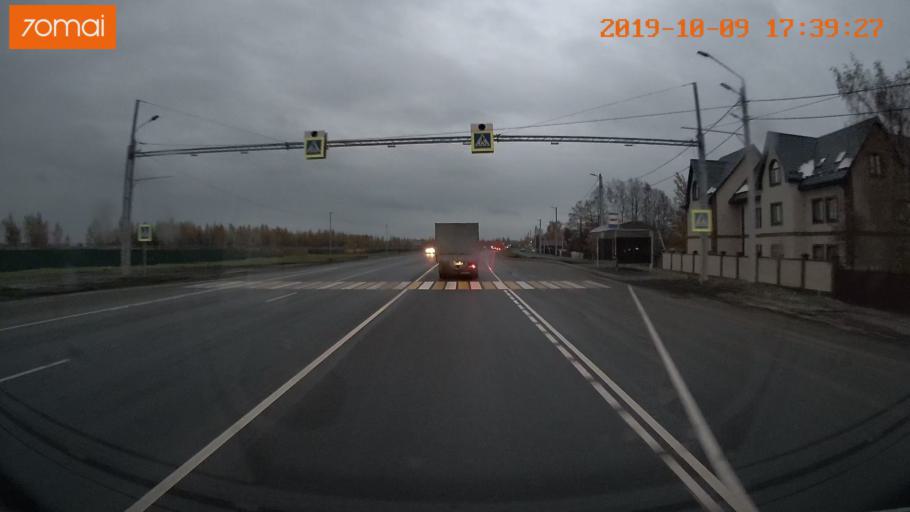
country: RU
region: Ivanovo
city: Bogorodskoye
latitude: 57.0605
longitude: 40.9586
